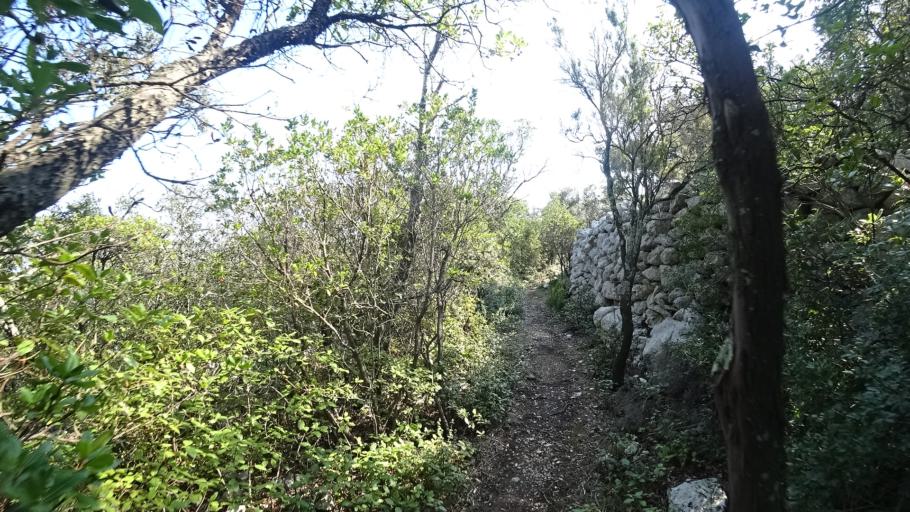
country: HR
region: Primorsko-Goranska
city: Mali Losinj
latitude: 44.4948
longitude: 14.5297
